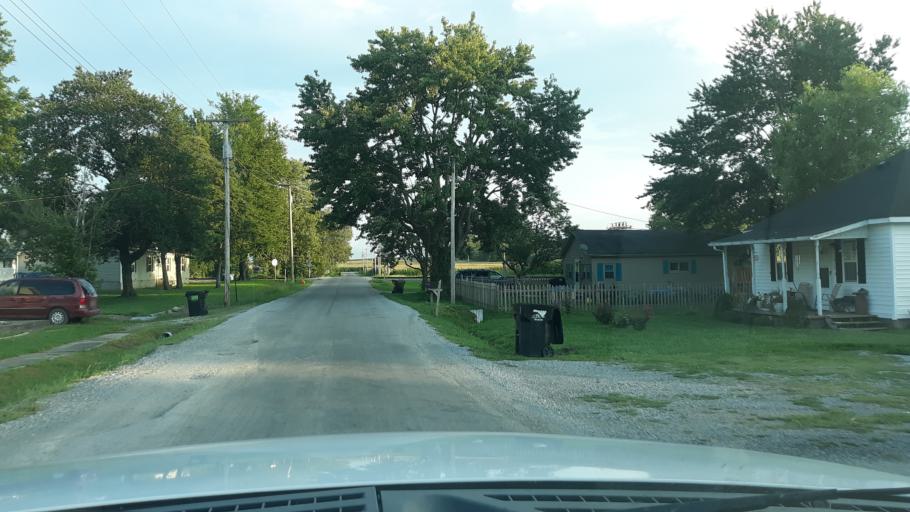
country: US
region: Illinois
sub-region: Saline County
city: Harrisburg
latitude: 37.8377
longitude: -88.6132
